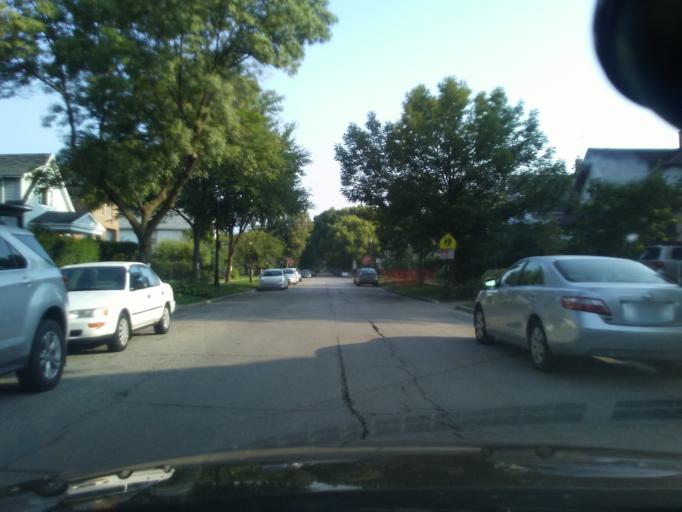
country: US
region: Illinois
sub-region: Cook County
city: Evanston
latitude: 42.0350
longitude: -87.6822
